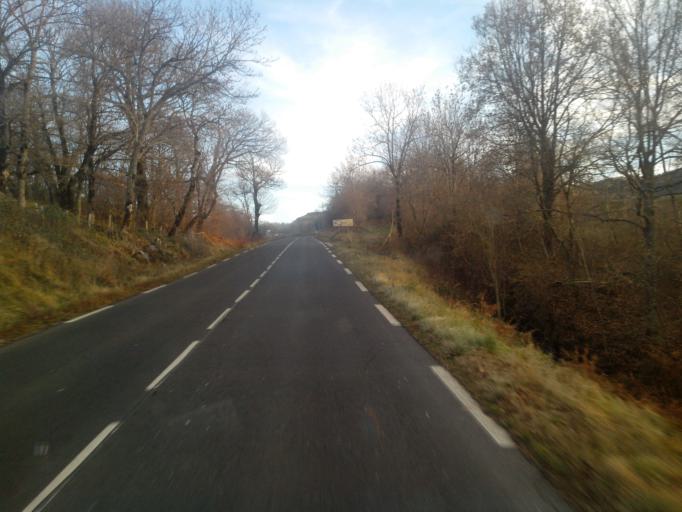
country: FR
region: Auvergne
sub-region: Departement du Cantal
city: Riom-es-Montagnes
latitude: 45.2682
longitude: 2.6691
